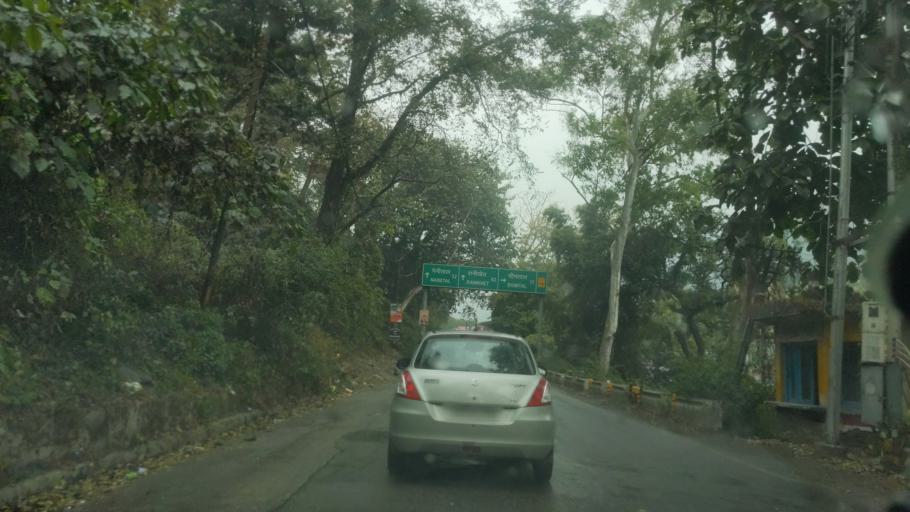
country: IN
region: Uttarakhand
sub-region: Naini Tal
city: Bhim Tal
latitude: 29.2891
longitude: 79.5466
